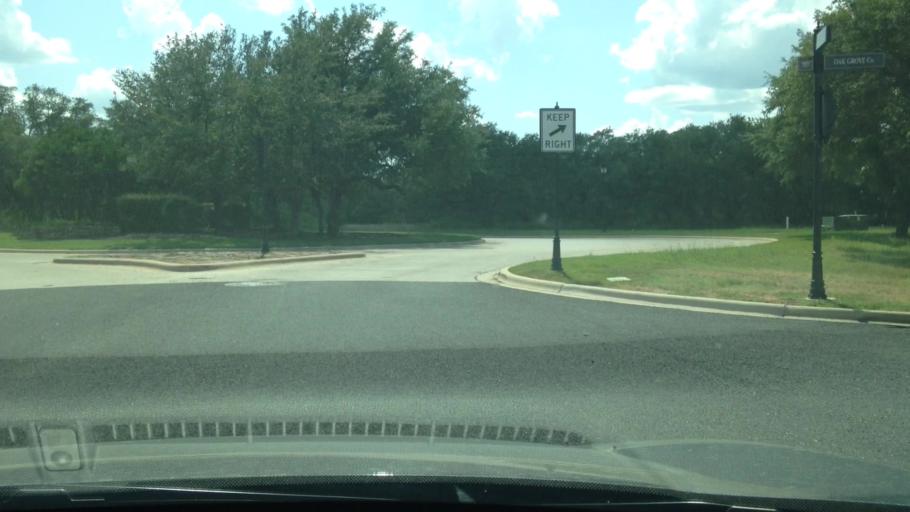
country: US
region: Texas
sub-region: Williamson County
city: Leander
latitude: 30.6397
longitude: -97.7962
